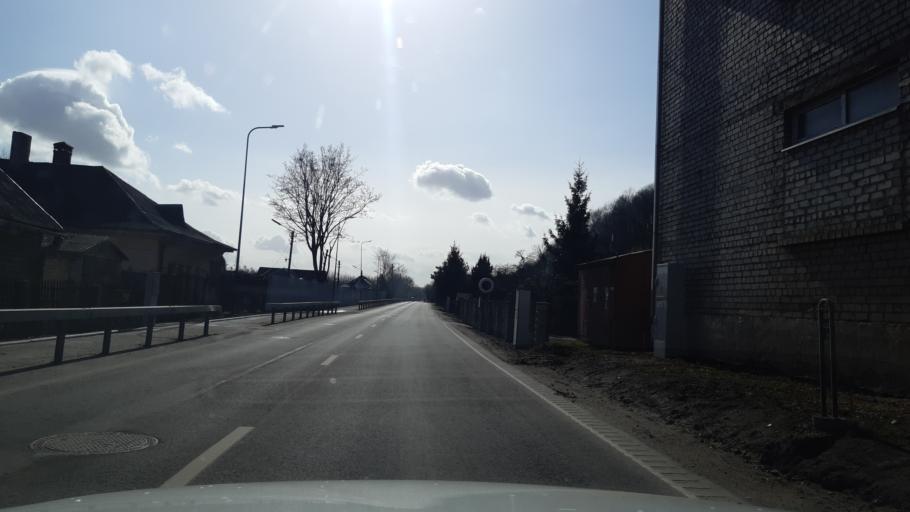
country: LT
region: Kauno apskritis
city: Dainava (Kaunas)
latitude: 54.8807
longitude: 23.9572
